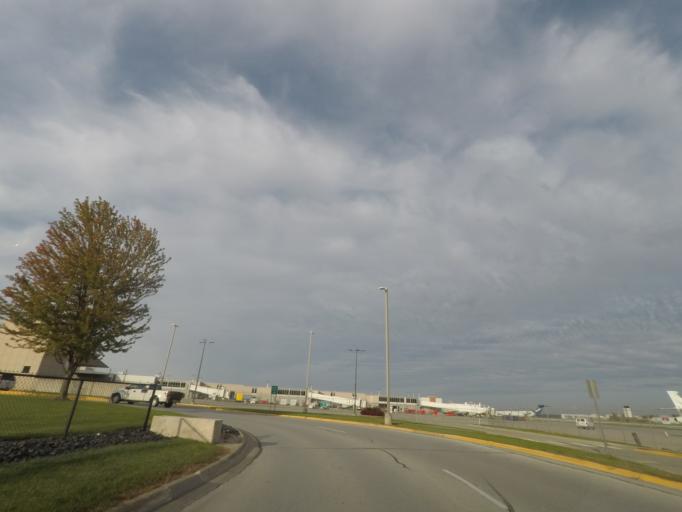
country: US
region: Iowa
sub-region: Warren County
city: Norwalk
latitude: 41.5343
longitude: -93.6477
